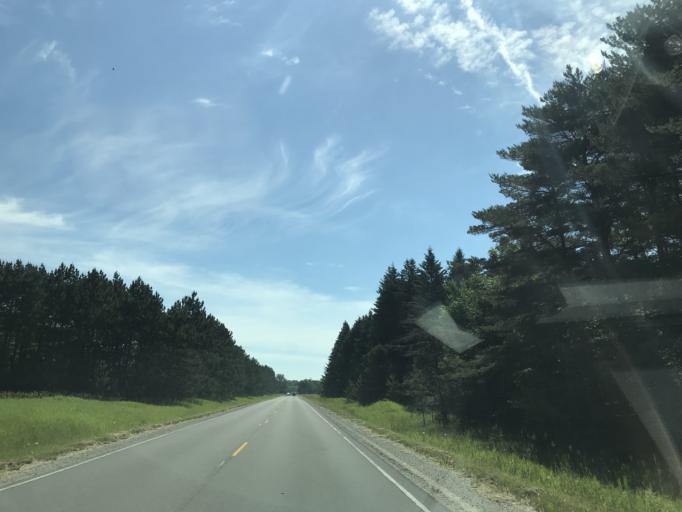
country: US
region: Michigan
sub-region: Grand Traverse County
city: Traverse City
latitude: 44.6542
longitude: -85.7076
